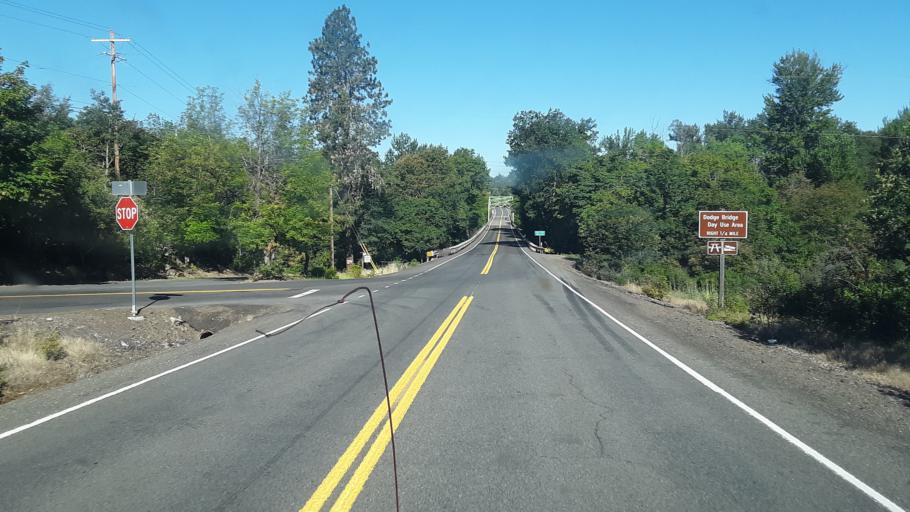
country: US
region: Oregon
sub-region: Jackson County
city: Eagle Point
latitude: 42.5244
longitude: -122.8387
